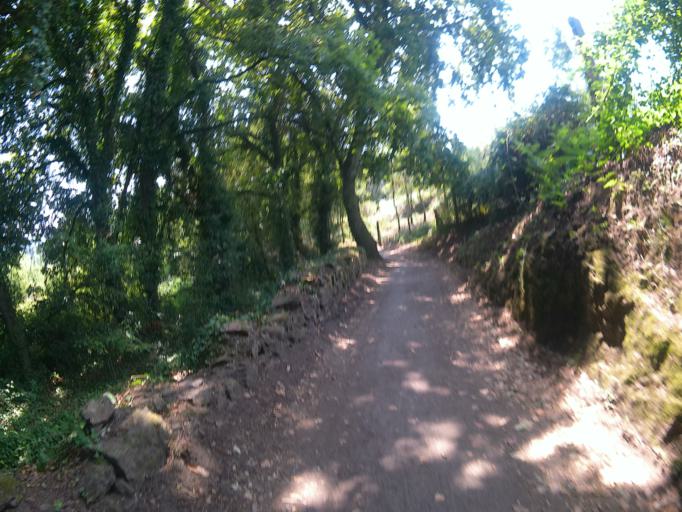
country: PT
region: Viana do Castelo
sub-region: Ponte de Lima
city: Ponte de Lima
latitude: 41.7754
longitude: -8.5700
